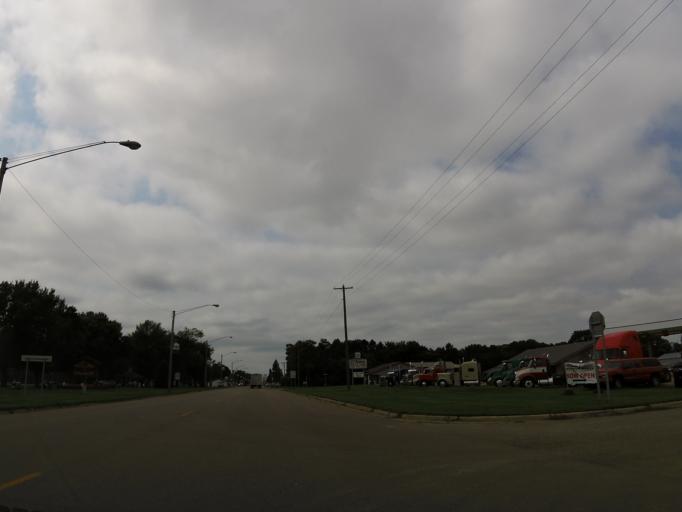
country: US
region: Minnesota
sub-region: Lac qui Parle County
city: Dawson
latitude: 44.9359
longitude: -96.0449
